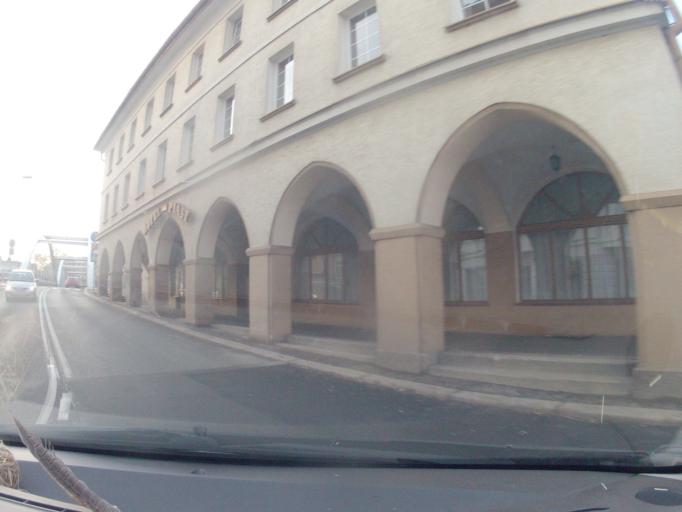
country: PL
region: Opole Voivodeship
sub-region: Powiat opolski
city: Opole
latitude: 50.6693
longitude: 17.9184
